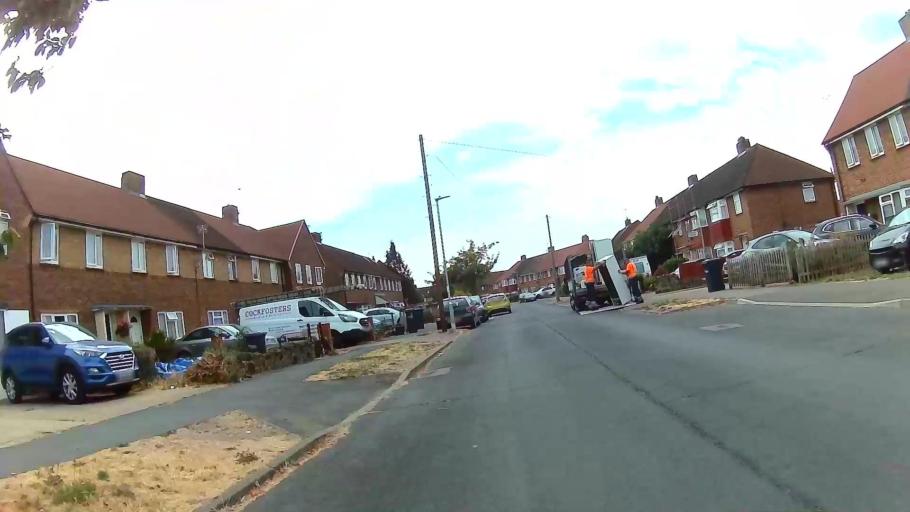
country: GB
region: England
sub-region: Hertfordshire
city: Waltham Cross
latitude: 51.6846
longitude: -0.0370
